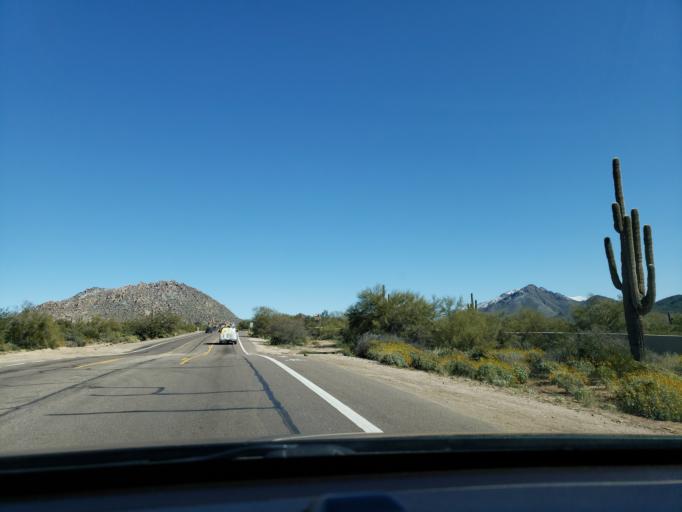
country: US
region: Arizona
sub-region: Maricopa County
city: Carefree
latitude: 33.7126
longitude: -111.8743
